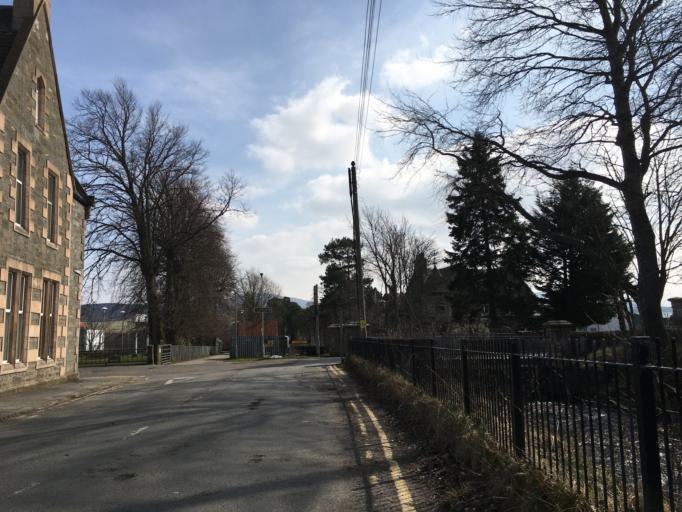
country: GB
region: Scotland
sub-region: Highland
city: Kingussie
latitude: 57.0790
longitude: -4.0523
